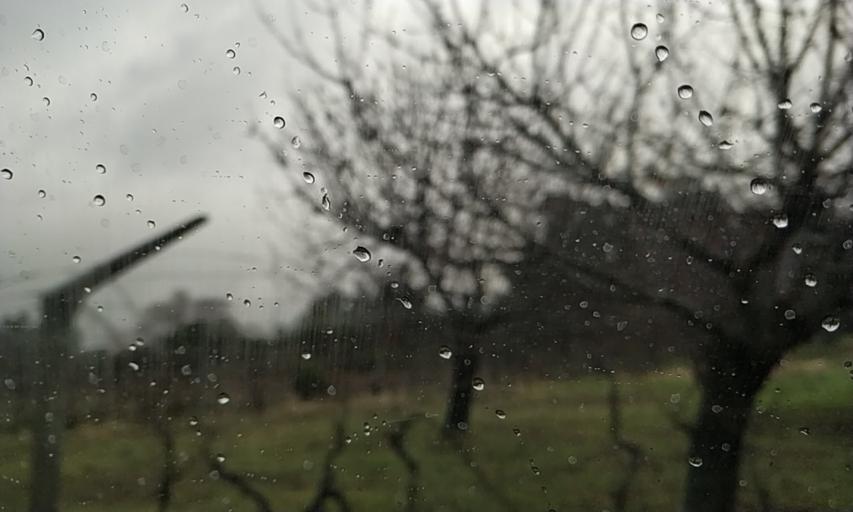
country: PT
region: Vila Real
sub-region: Murca
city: Murca
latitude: 41.3992
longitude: -7.4878
